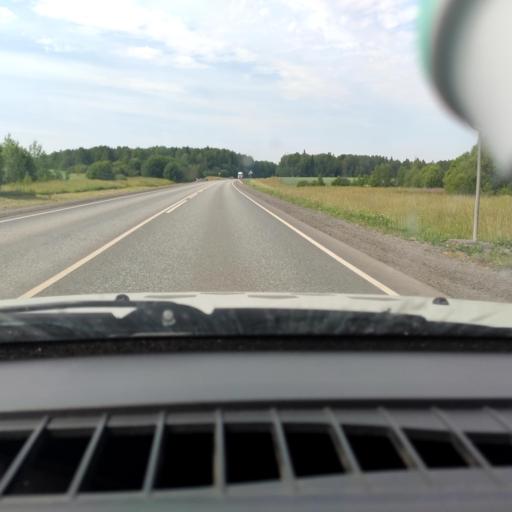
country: RU
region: Perm
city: Siva
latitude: 58.4924
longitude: 54.0532
